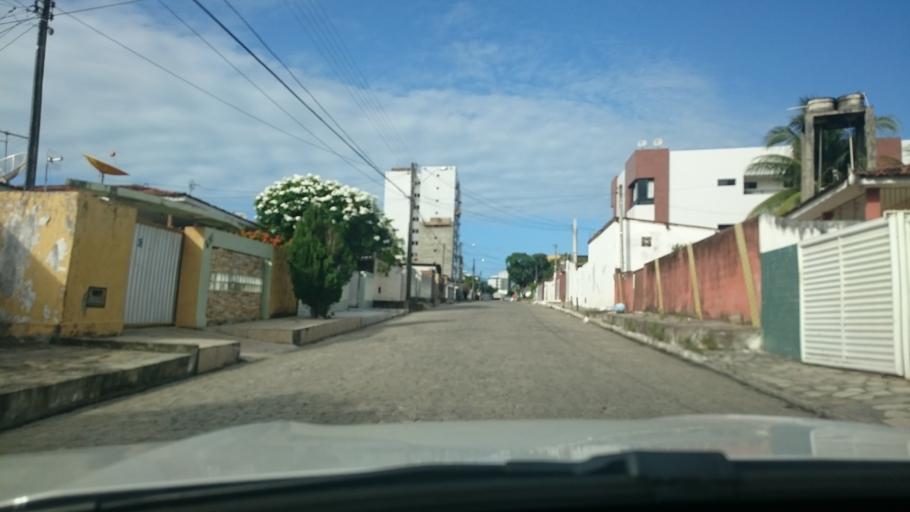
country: BR
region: Paraiba
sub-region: Joao Pessoa
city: Joao Pessoa
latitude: -7.1531
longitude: -34.8429
